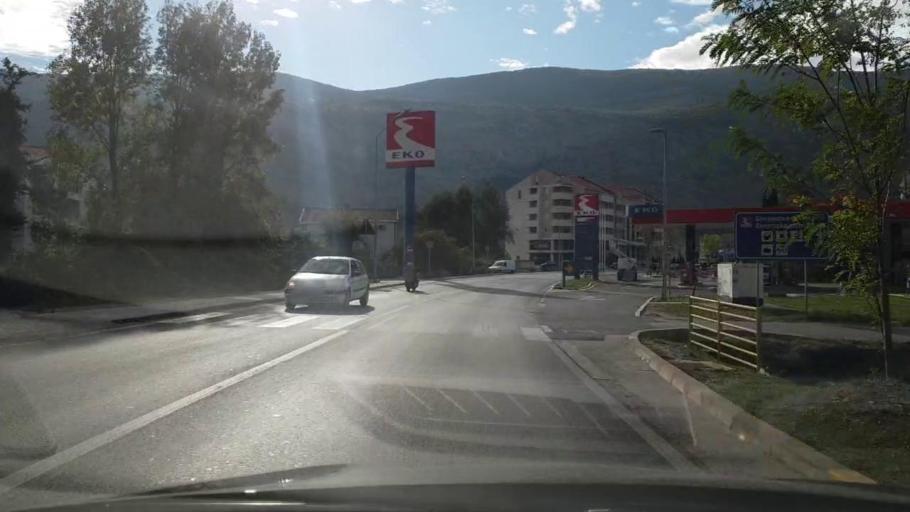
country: ME
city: Igalo
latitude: 42.4558
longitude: 18.5044
